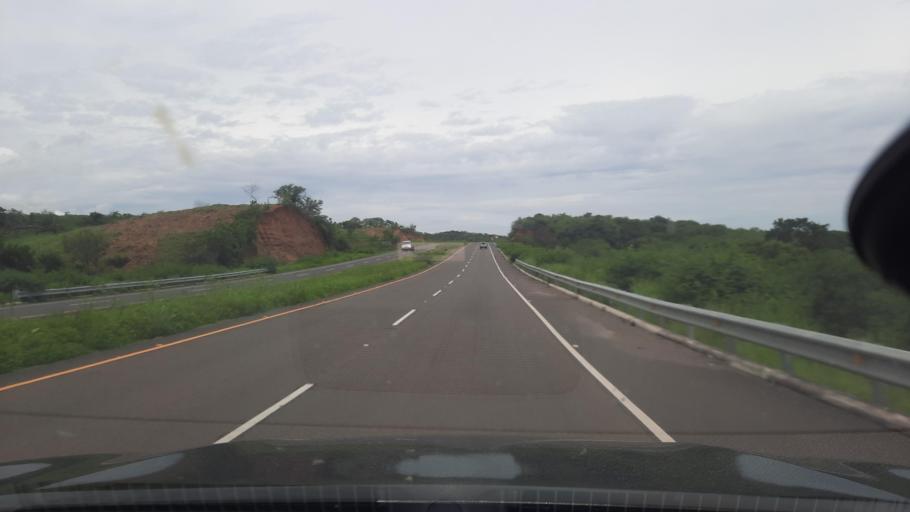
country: HN
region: Valle
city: Aramecina
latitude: 13.7446
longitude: -87.7181
